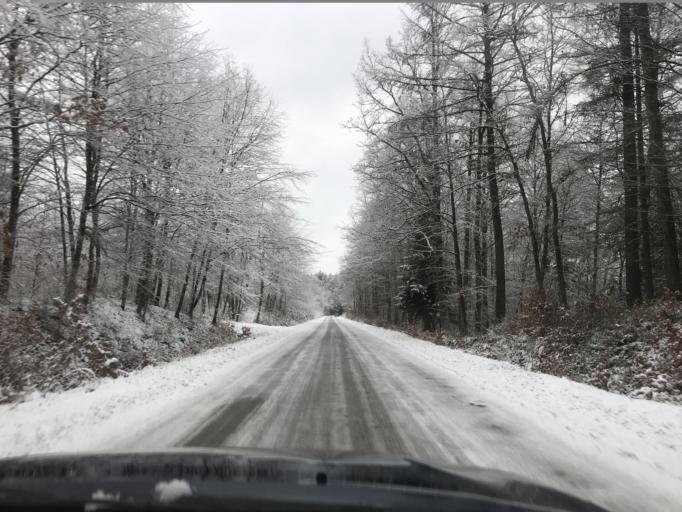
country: PL
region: Pomeranian Voivodeship
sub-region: Powiat bytowski
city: Parchowo
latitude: 54.2451
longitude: 17.5776
